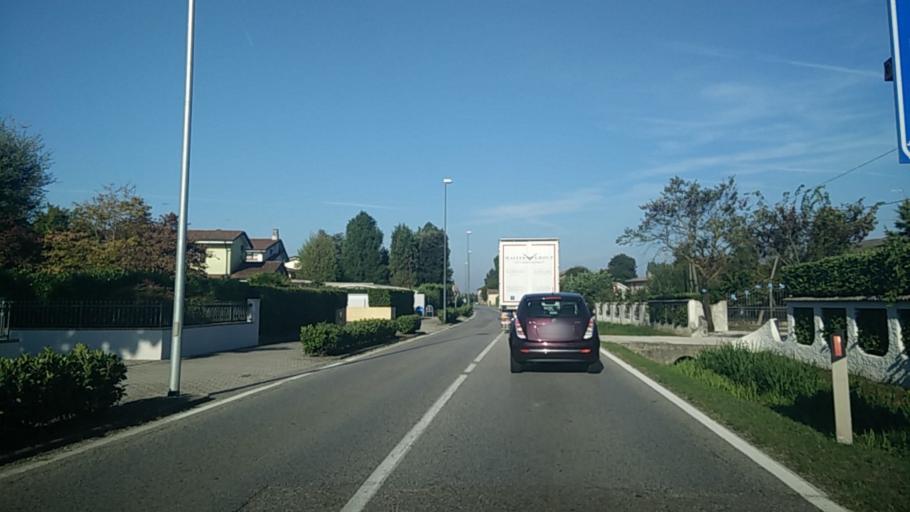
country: IT
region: Veneto
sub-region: Provincia di Venezia
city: Scorze
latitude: 45.5756
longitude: 12.1011
